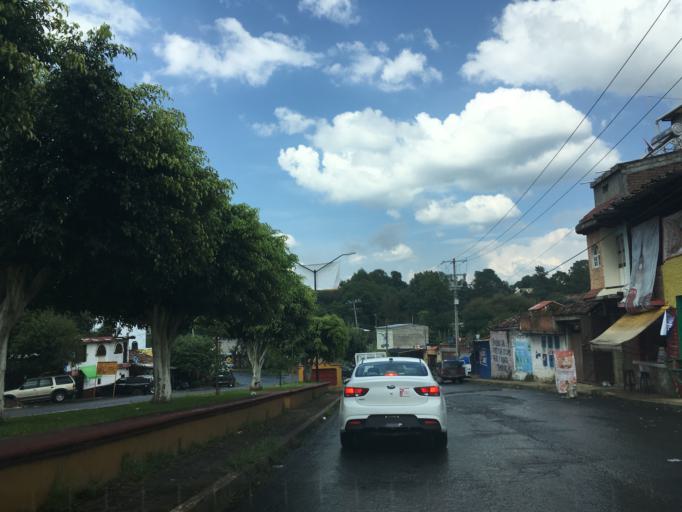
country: MX
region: Michoacan
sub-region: Tingueindin
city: Tingueindin
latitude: 19.7418
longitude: -102.4841
